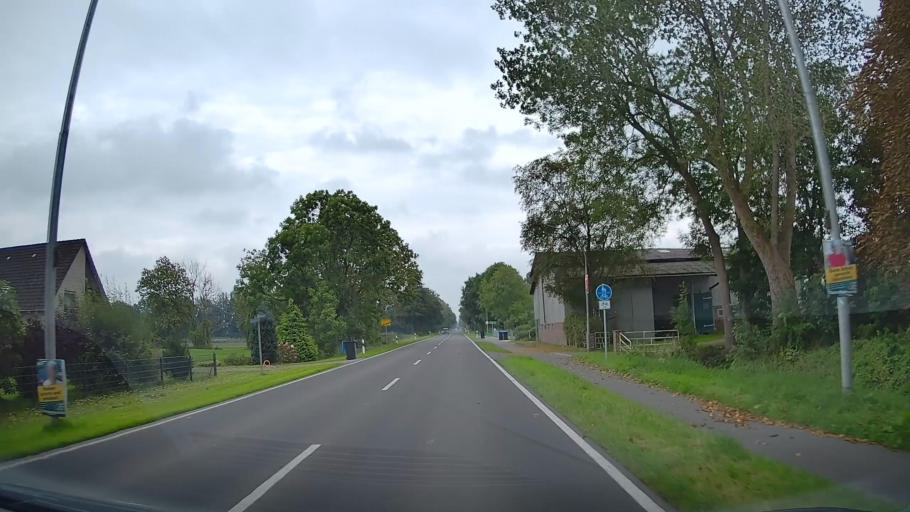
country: DE
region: Lower Saxony
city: Drochtersen
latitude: 53.7297
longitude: 9.3525
